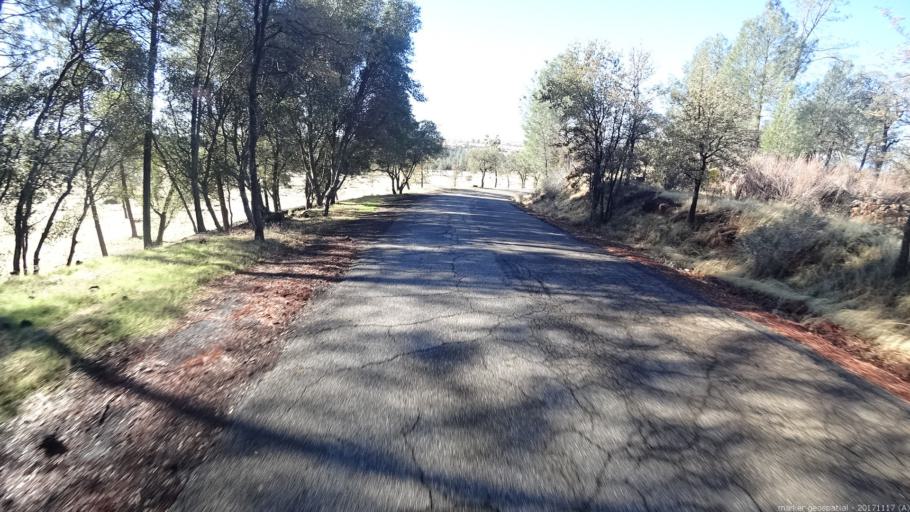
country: US
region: California
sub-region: Shasta County
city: Cottonwood
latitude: 40.4383
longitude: -122.1202
